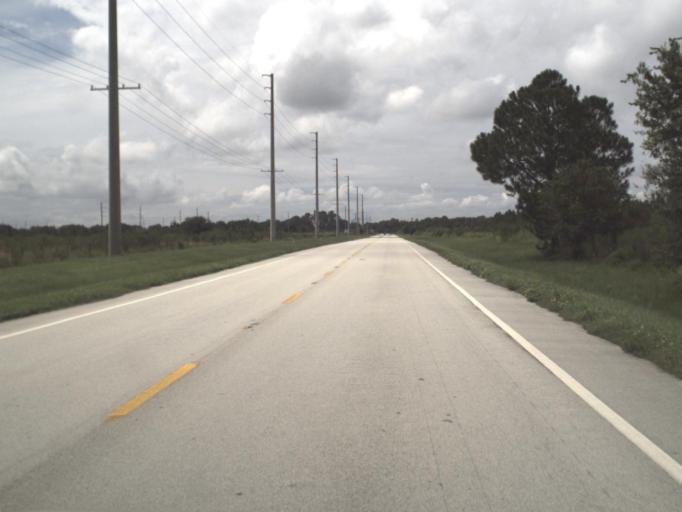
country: US
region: Florida
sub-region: Hardee County
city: Bowling Green
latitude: 27.5952
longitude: -82.0454
